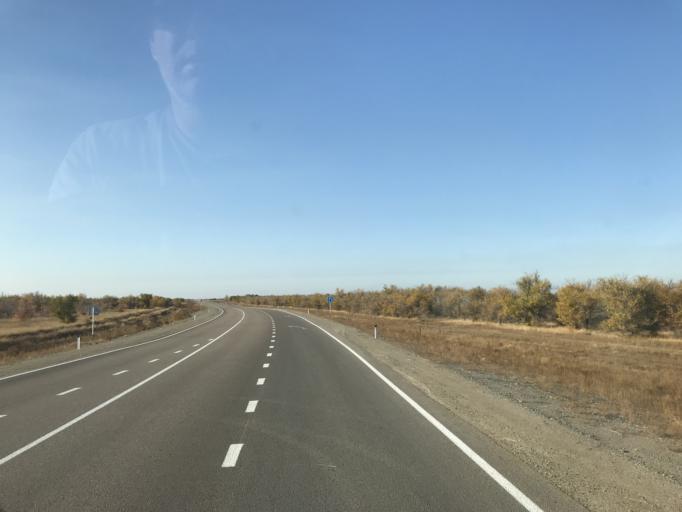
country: KZ
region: Pavlodar
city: Koktobe
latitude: 51.7292
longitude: 77.5588
